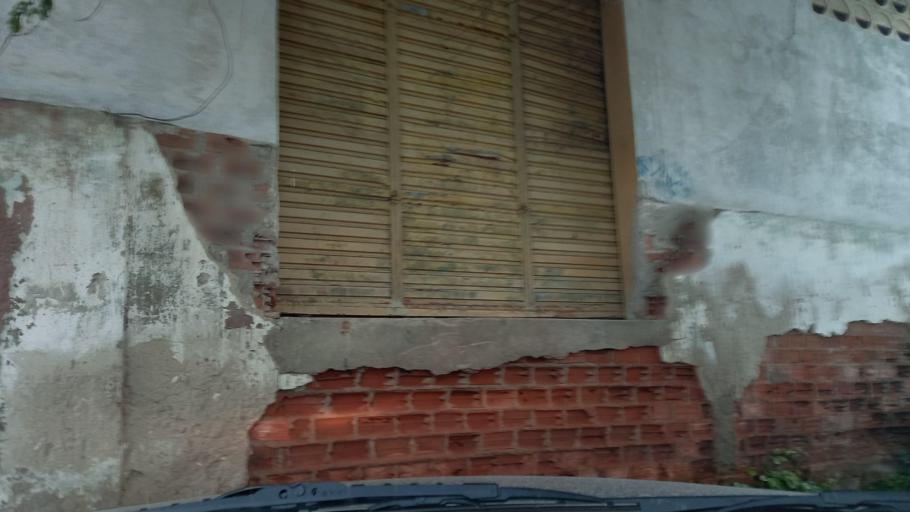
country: BR
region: Pernambuco
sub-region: Caruaru
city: Caruaru
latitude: -8.2917
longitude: -35.9821
